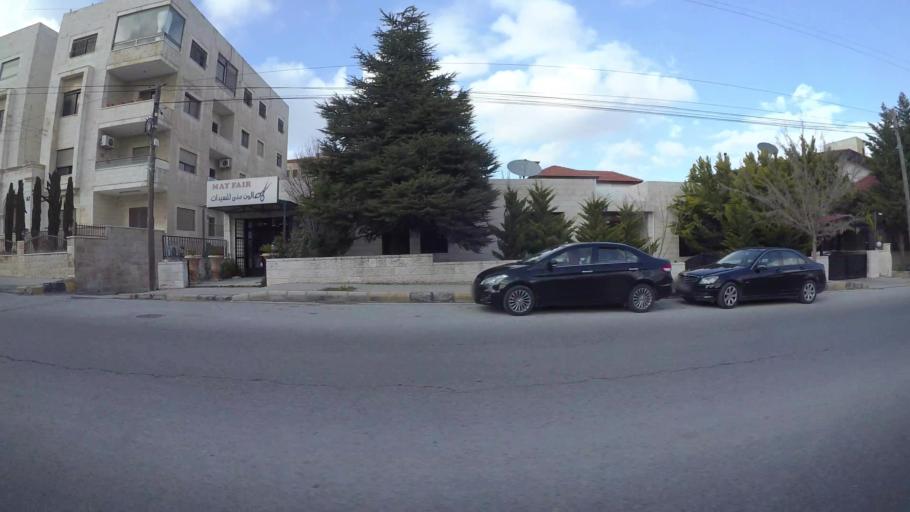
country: JO
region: Amman
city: Wadi as Sir
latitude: 31.9786
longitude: 35.8524
